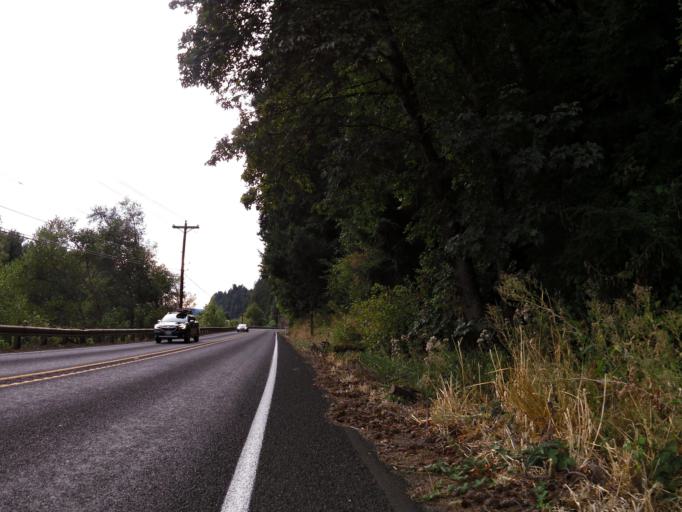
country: US
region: Washington
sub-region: Cowlitz County
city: West Longview
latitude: 46.1913
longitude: -123.1132
